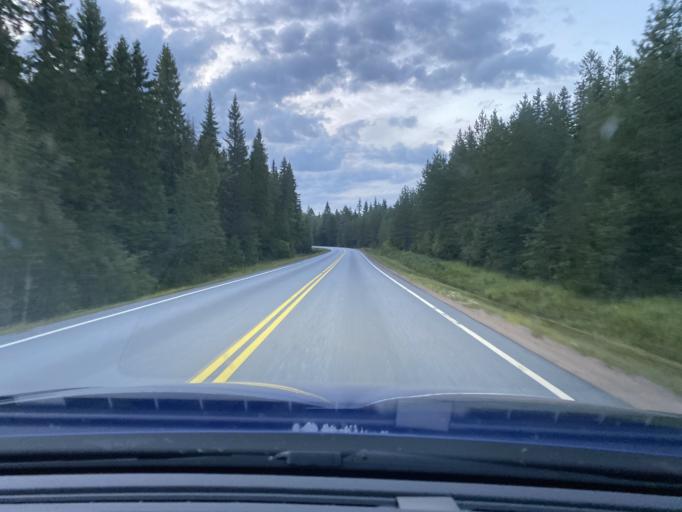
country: FI
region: Southern Ostrobothnia
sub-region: Suupohja
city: Kauhajoki
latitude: 62.2496
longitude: 22.2723
